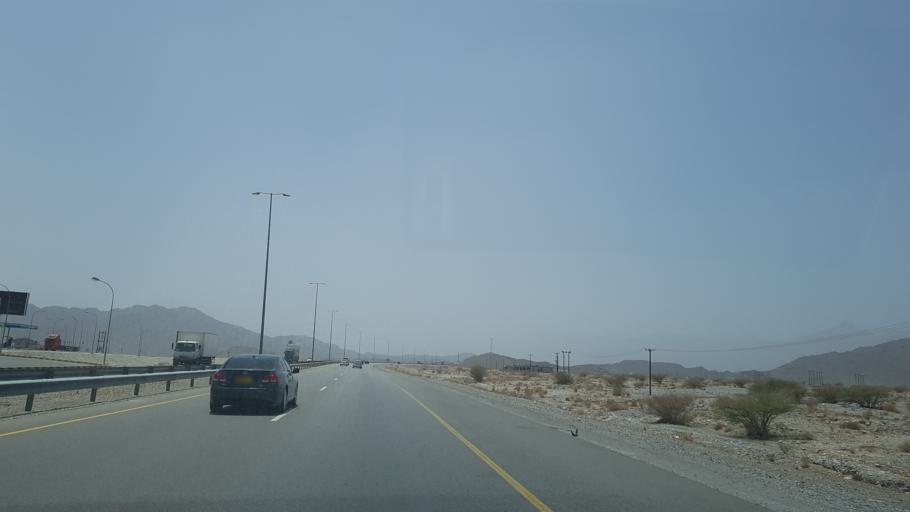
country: OM
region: Muhafazat ad Dakhiliyah
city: Bidbid
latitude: 23.3862
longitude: 58.0593
